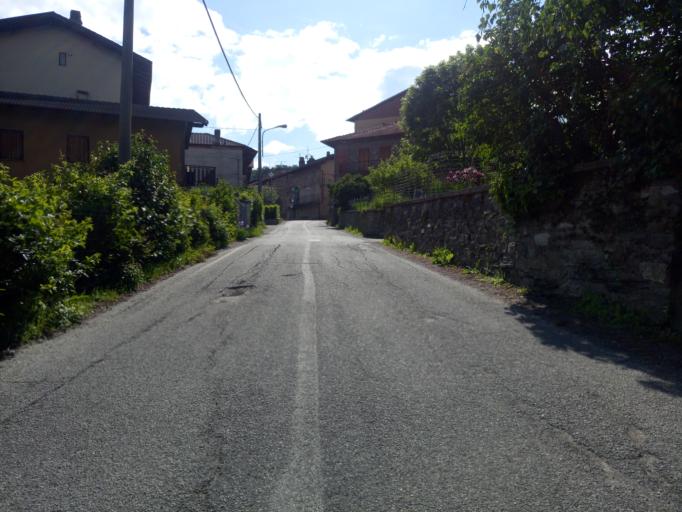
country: IT
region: Piedmont
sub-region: Provincia di Torino
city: Meana di Susa
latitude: 45.1225
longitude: 7.0685
